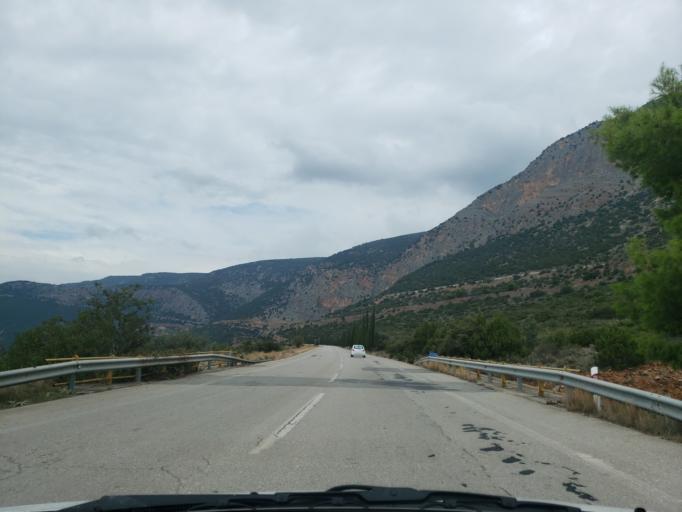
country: GR
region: Central Greece
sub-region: Nomos Fokidos
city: Delphi
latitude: 38.4866
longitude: 22.4605
